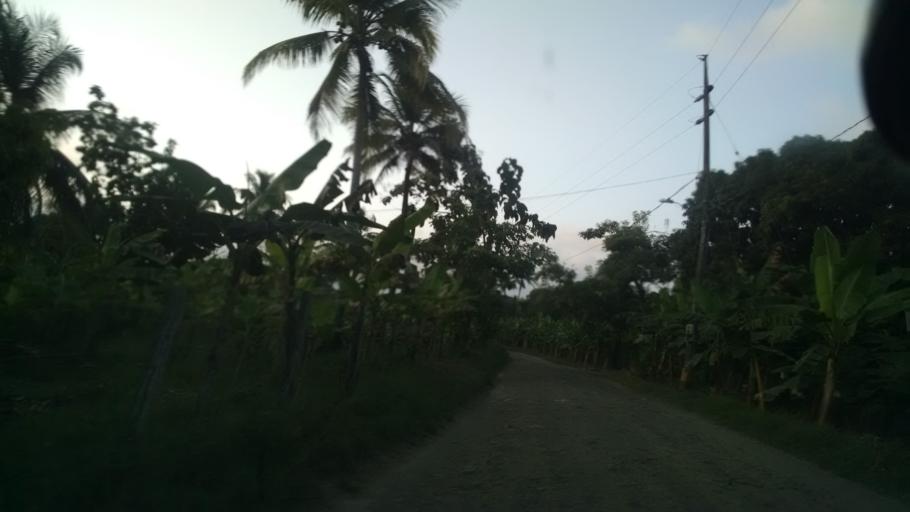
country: CO
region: Antioquia
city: San Juan de Uraba
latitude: 8.7206
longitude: -76.6006
